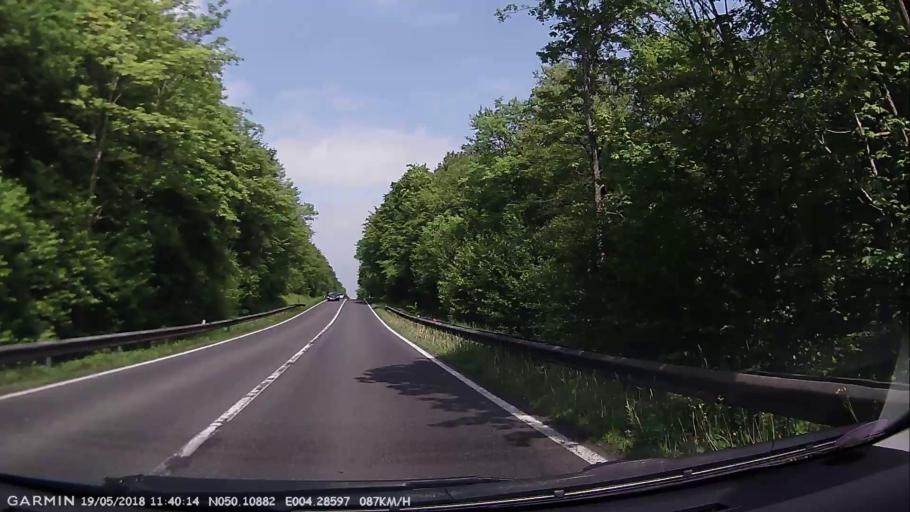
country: BE
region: Wallonia
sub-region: Province du Hainaut
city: Froidchapelle
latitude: 50.1092
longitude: 4.2859
